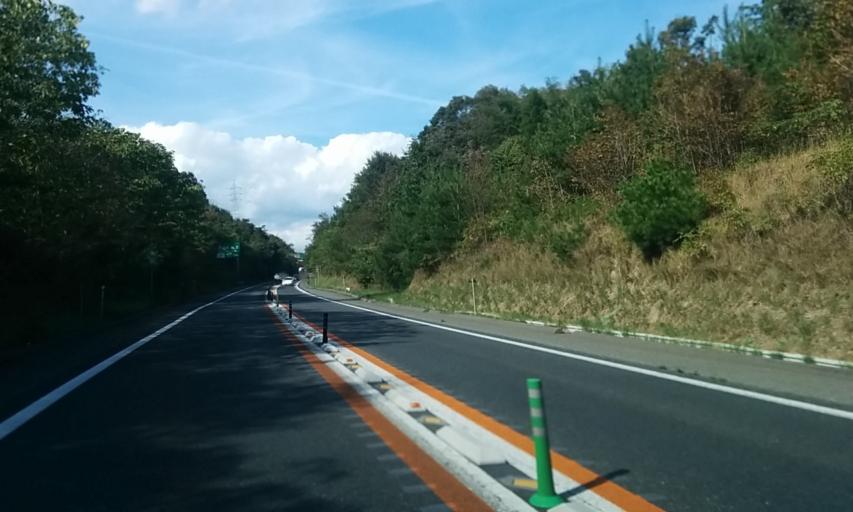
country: JP
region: Kyoto
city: Tanabe
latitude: 34.7964
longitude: 135.7584
